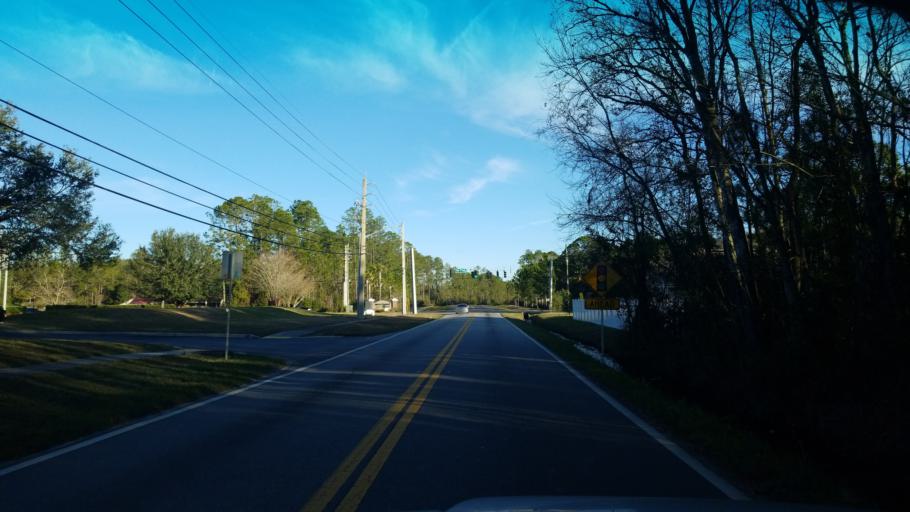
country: US
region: Florida
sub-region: Duval County
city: Baldwin
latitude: 30.3315
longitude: -81.8486
